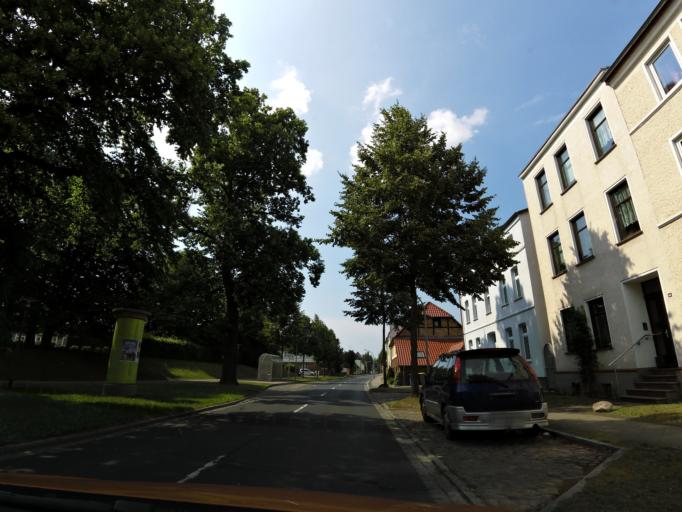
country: DE
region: Mecklenburg-Vorpommern
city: Guestrow
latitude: 53.7854
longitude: 12.1859
